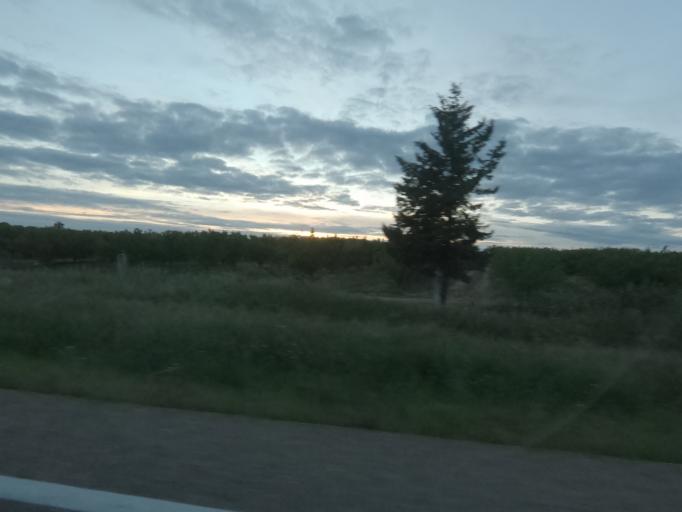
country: ES
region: Extremadura
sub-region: Provincia de Badajoz
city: Badajoz
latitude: 38.9436
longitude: -6.9182
